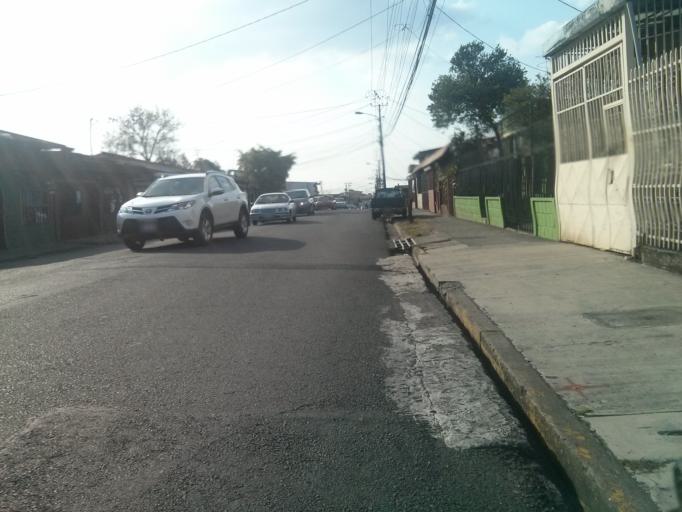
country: CR
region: San Jose
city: San Jose
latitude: 9.9089
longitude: -84.0707
